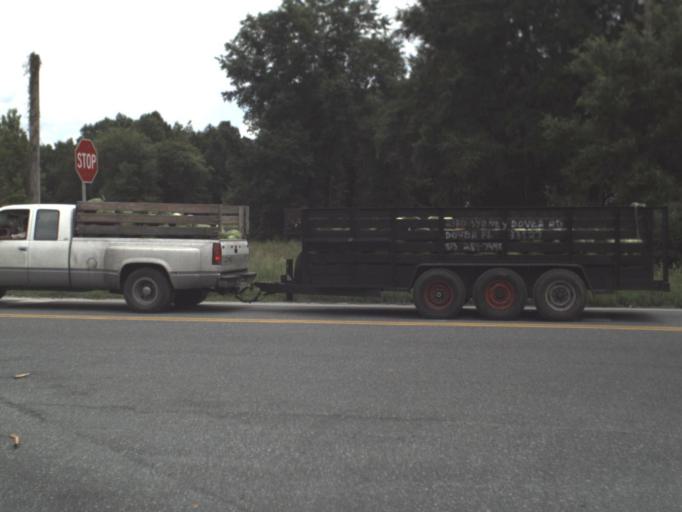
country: US
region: Florida
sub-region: Suwannee County
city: Wellborn
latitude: 29.9978
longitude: -82.8614
